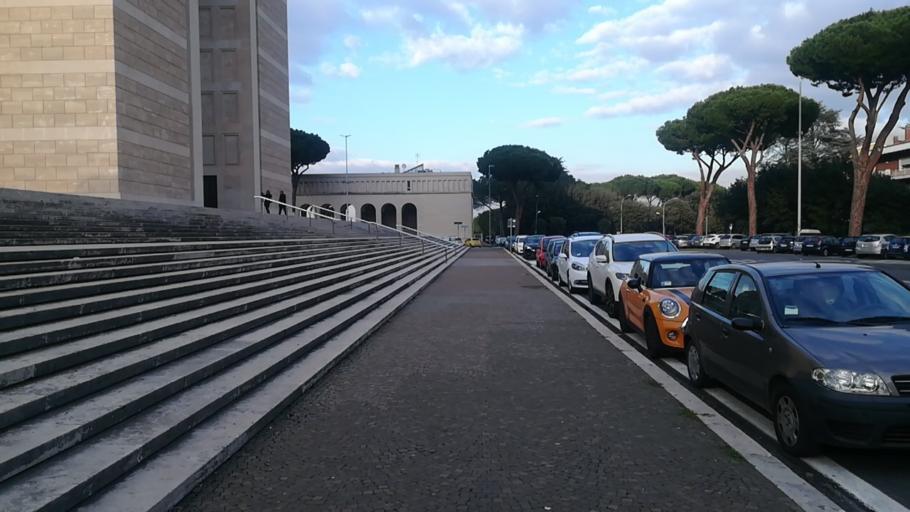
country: IT
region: Latium
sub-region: Citta metropolitana di Roma Capitale
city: Vitinia
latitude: 41.8332
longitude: 12.4596
